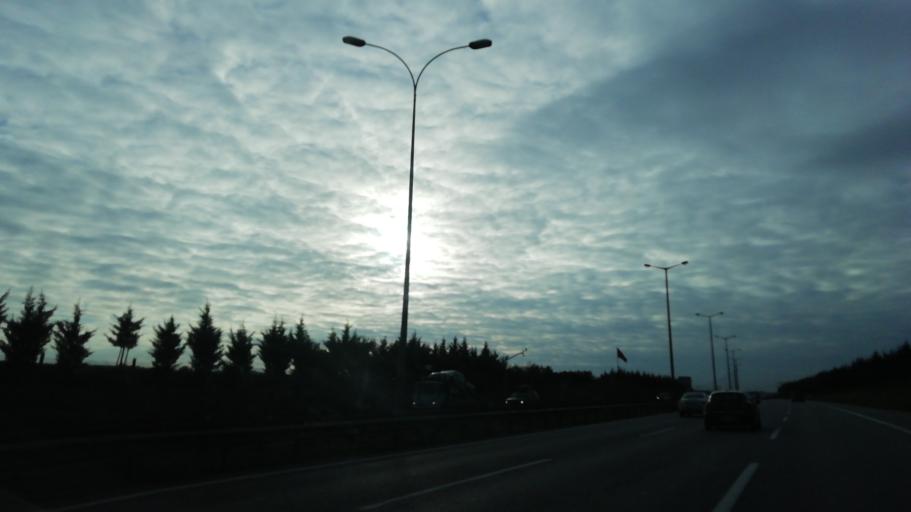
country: TR
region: Istanbul
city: Icmeler
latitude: 40.9203
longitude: 29.3516
